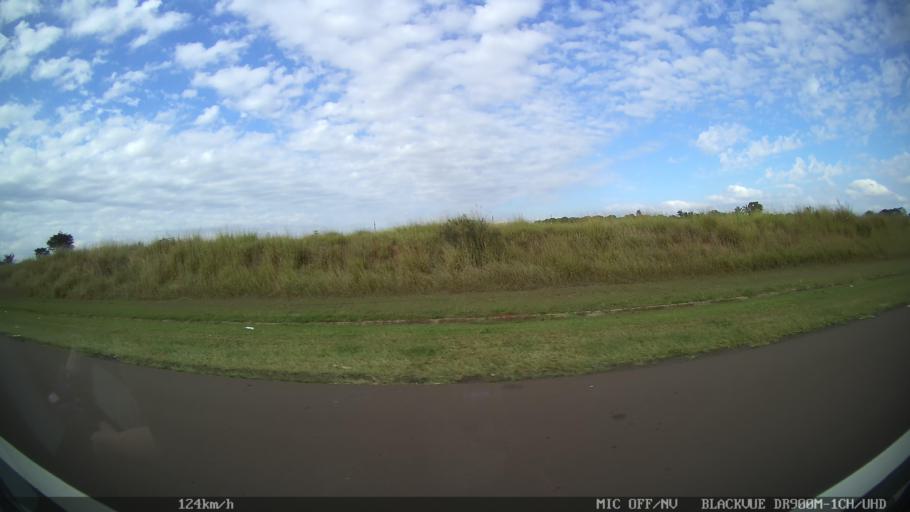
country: BR
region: Sao Paulo
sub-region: Iracemapolis
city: Iracemapolis
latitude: -22.6081
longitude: -47.4595
